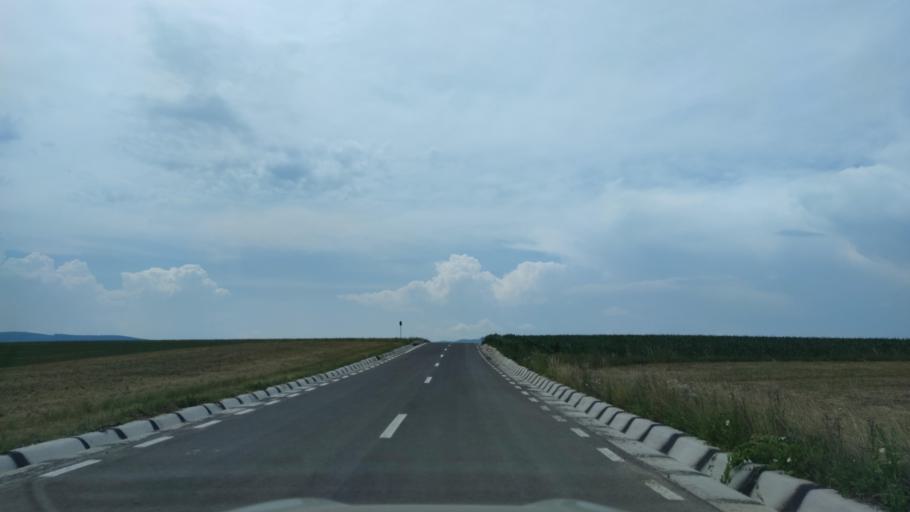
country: RO
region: Harghita
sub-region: Comuna Subcetate
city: Subcetate
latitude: 46.8181
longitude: 25.4521
